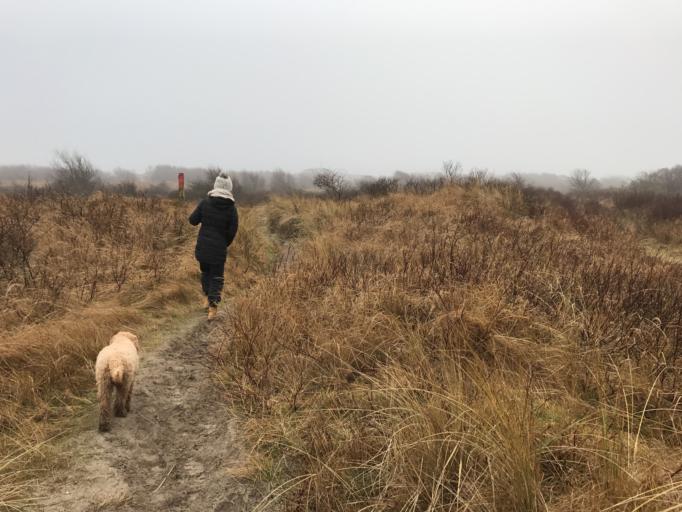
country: DE
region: Lower Saxony
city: Borkum
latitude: 53.6096
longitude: 6.7353
